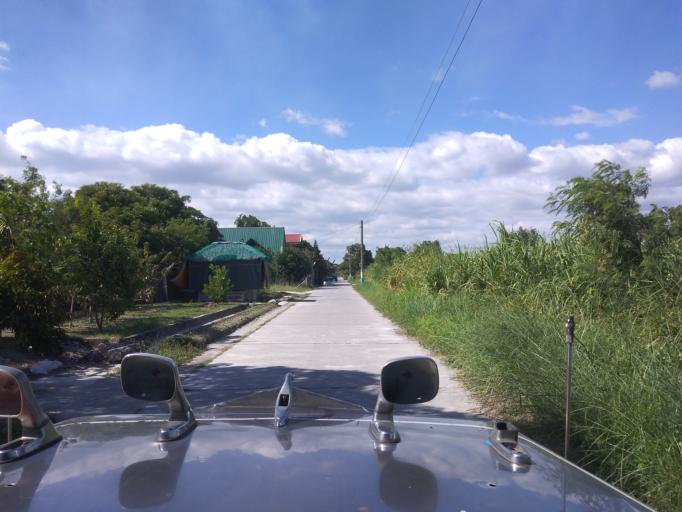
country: PH
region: Central Luzon
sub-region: Province of Pampanga
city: Magliman
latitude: 15.0266
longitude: 120.6334
